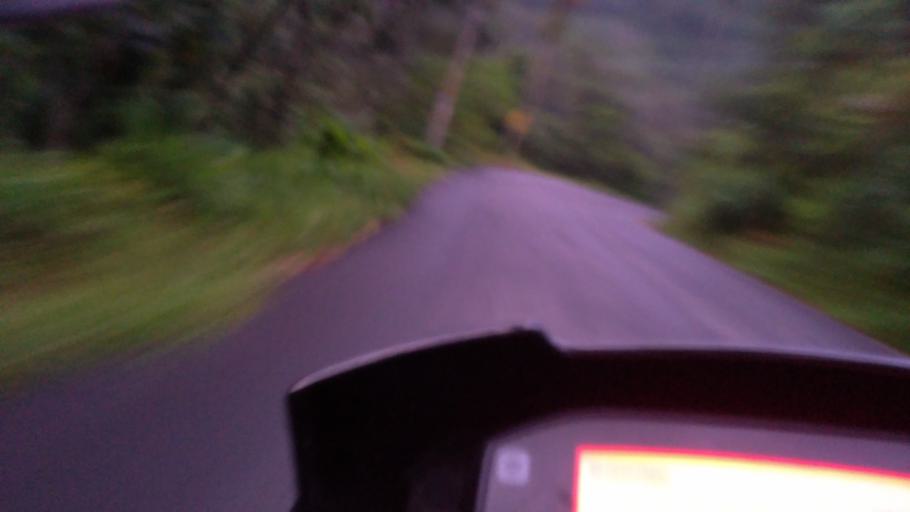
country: IN
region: Kerala
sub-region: Idukki
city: Munnar
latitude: 9.9628
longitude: 77.0691
